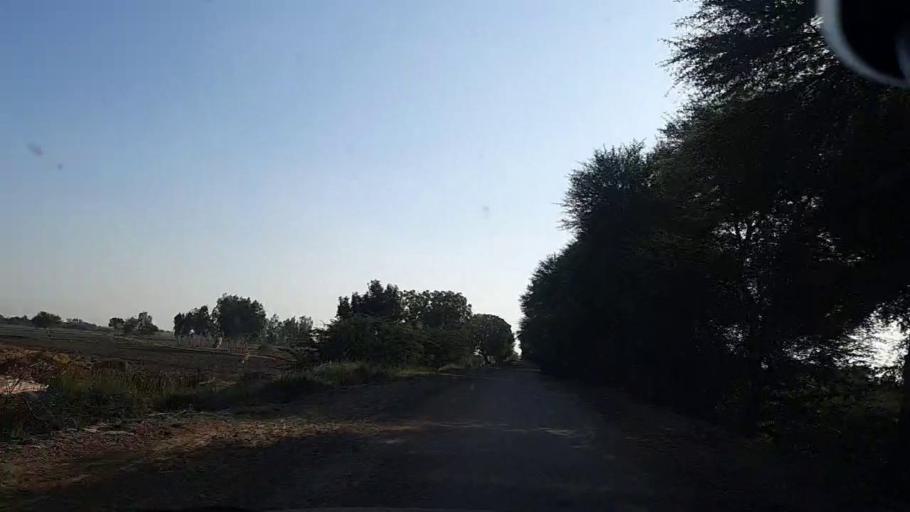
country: PK
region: Sindh
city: Chuhar Jamali
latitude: 24.5635
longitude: 68.0405
